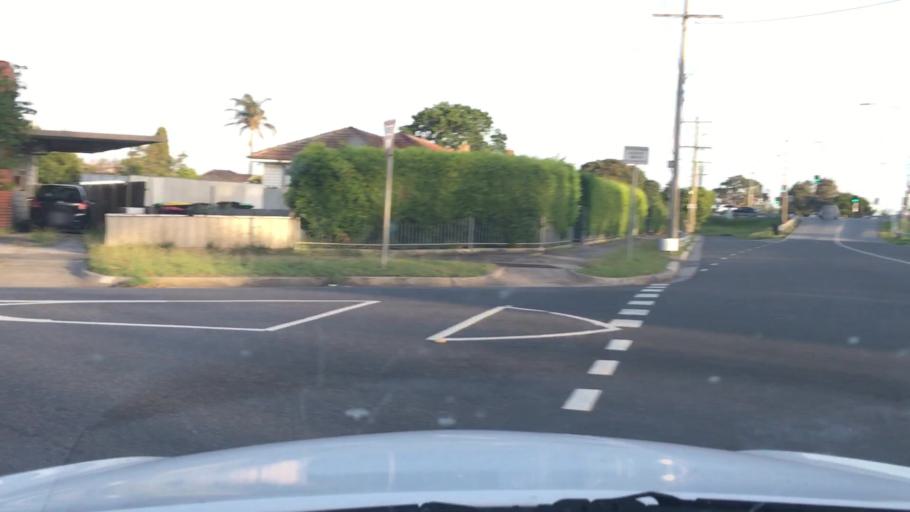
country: AU
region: Victoria
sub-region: Greater Dandenong
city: Dandenong
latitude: -37.9830
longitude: 145.1993
